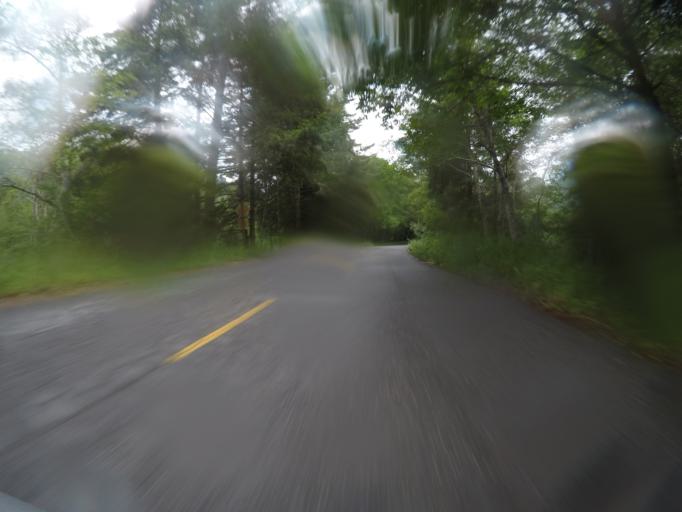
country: US
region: California
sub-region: Humboldt County
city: Westhaven-Moonstone
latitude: 41.3007
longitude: -124.0403
